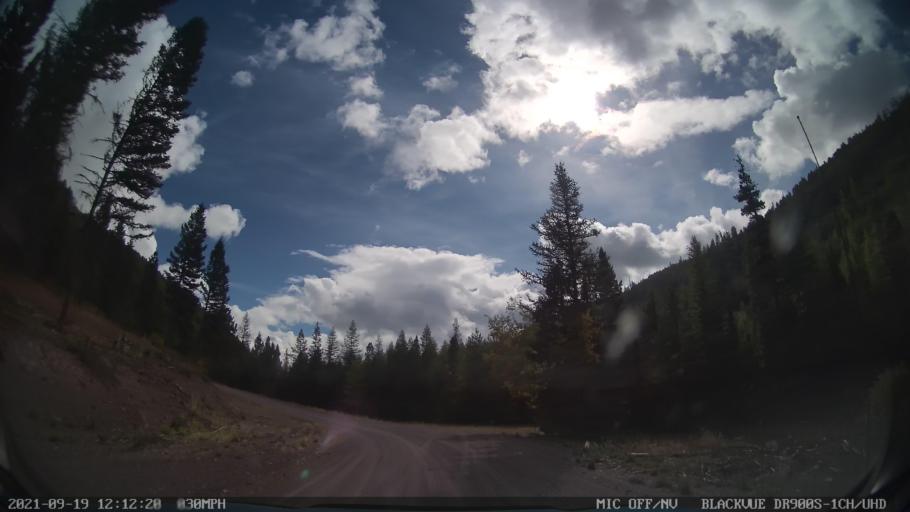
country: US
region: Montana
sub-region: Missoula County
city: Seeley Lake
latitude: 47.1712
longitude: -113.3670
